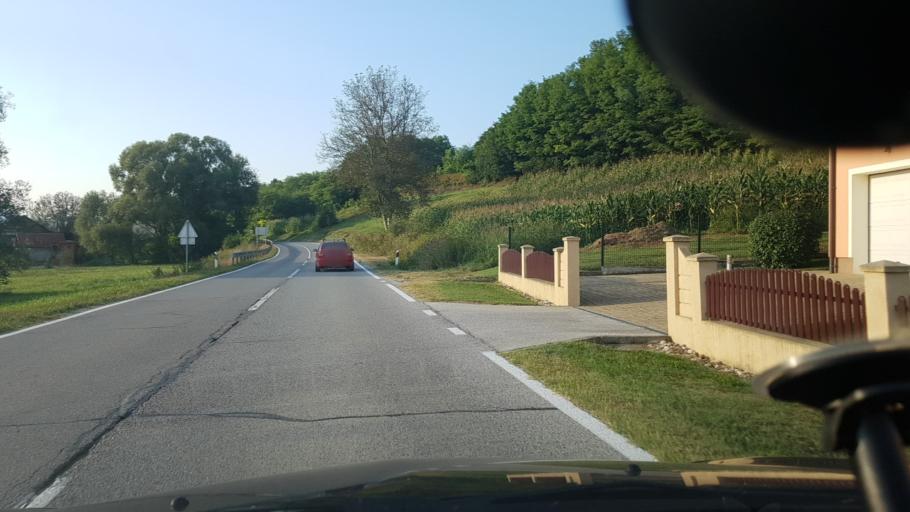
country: HR
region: Krapinsko-Zagorska
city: Pregrada
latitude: 46.1230
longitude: 15.8050
